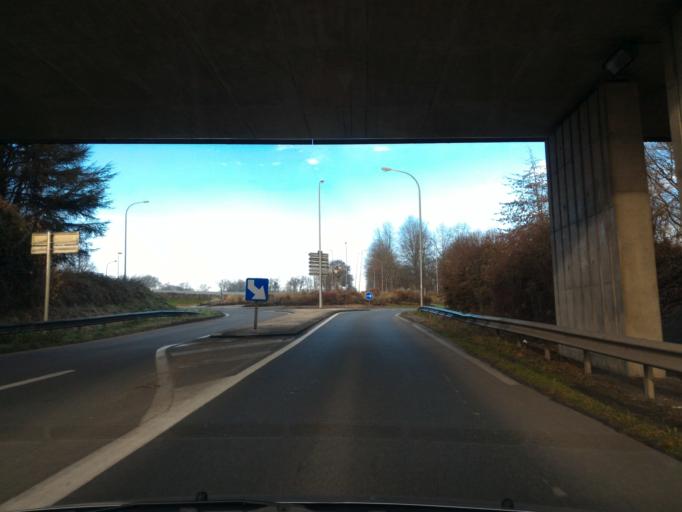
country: FR
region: Poitou-Charentes
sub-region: Departement de la Charente
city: Confolens
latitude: 46.0236
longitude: 0.6539
